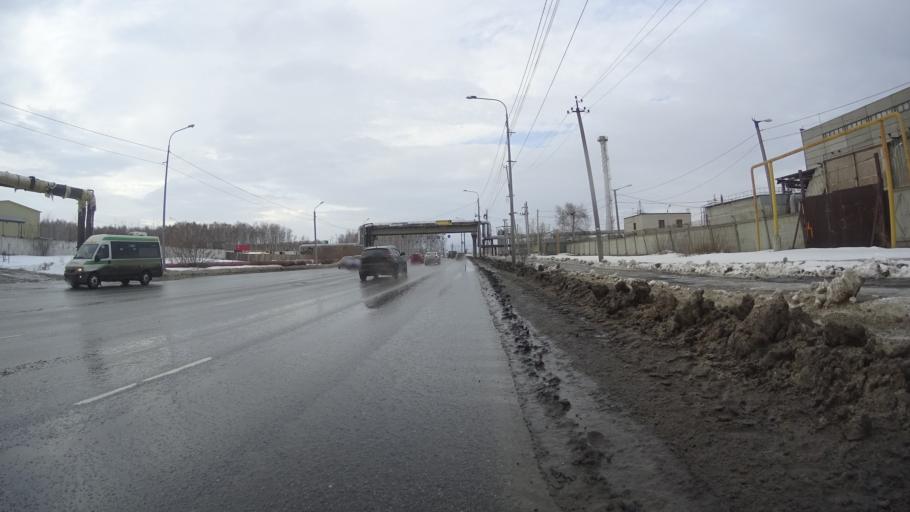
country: RU
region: Chelyabinsk
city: Roshchino
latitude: 55.2071
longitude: 61.3194
